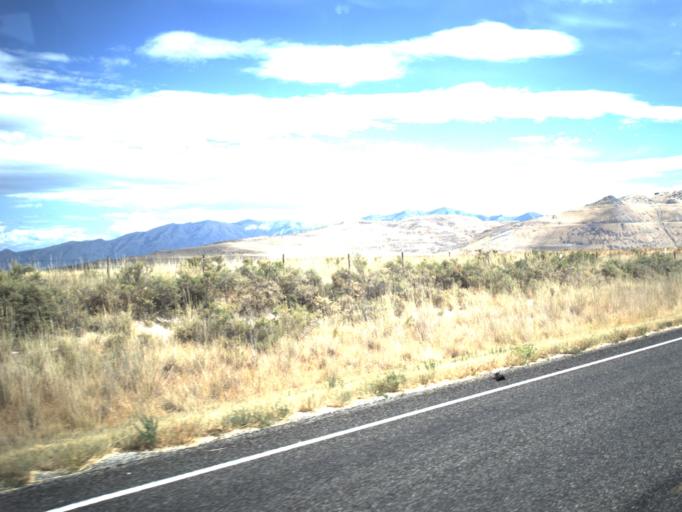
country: US
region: Utah
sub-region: Box Elder County
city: Tremonton
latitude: 41.6053
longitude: -112.3186
